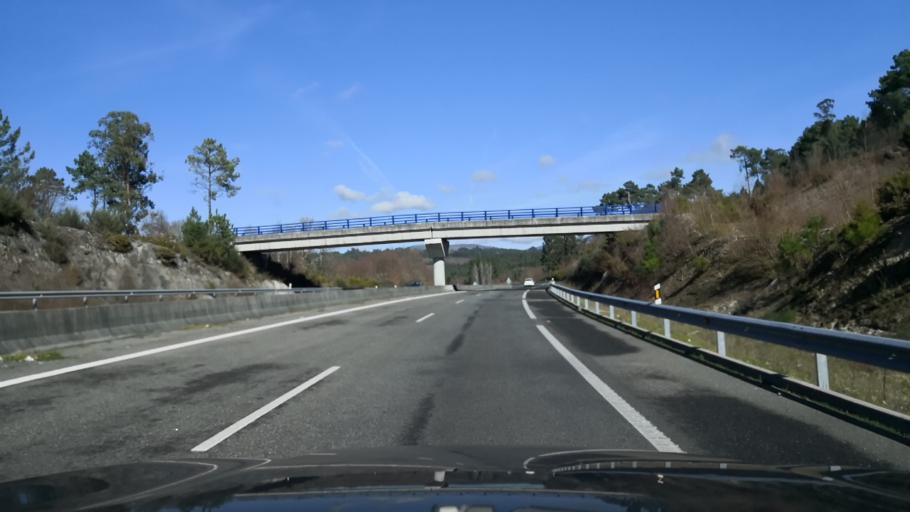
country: ES
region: Galicia
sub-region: Provincia de Ourense
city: Pinor
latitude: 42.4779
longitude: -8.0253
